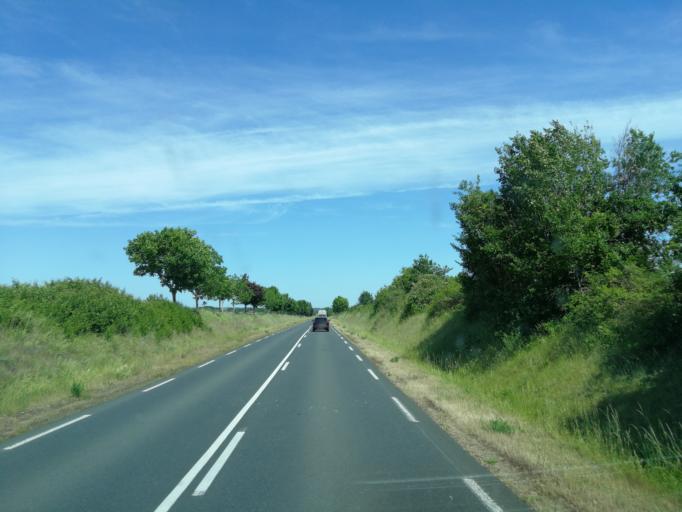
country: FR
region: Poitou-Charentes
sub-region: Departement des Deux-Sevres
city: Saint-Leger-de-Montbrun
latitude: 46.9736
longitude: -0.0791
